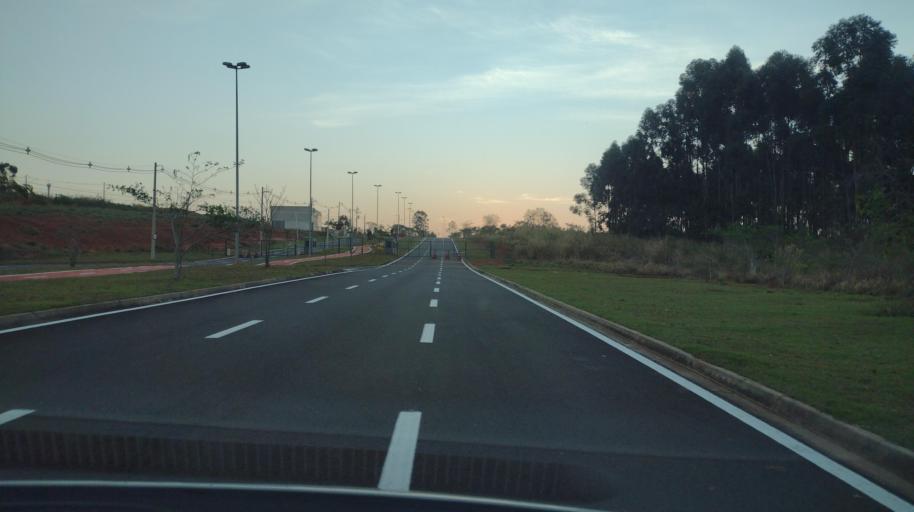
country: BR
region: Sao Paulo
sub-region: Sorocaba
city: Sorocaba
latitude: -23.3842
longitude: -47.4746
